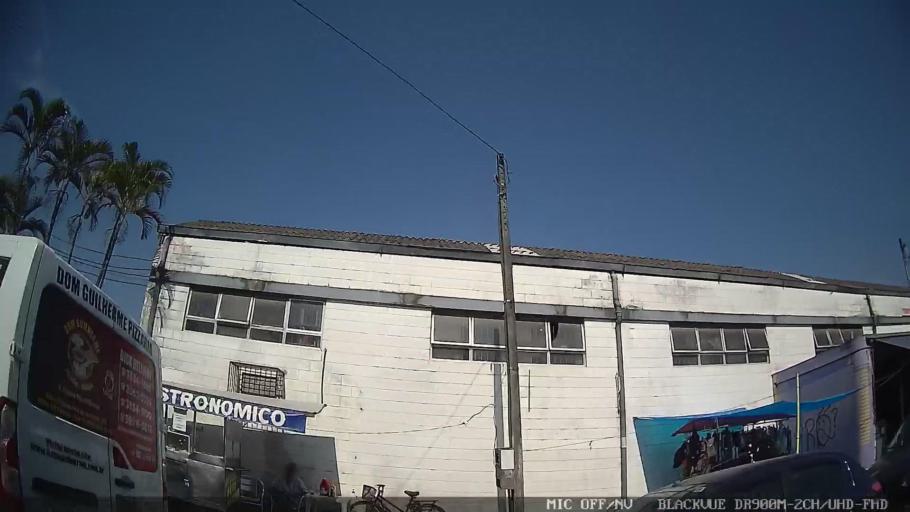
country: BR
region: Sao Paulo
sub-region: Guaruja
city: Guaruja
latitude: -23.9838
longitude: -46.2681
